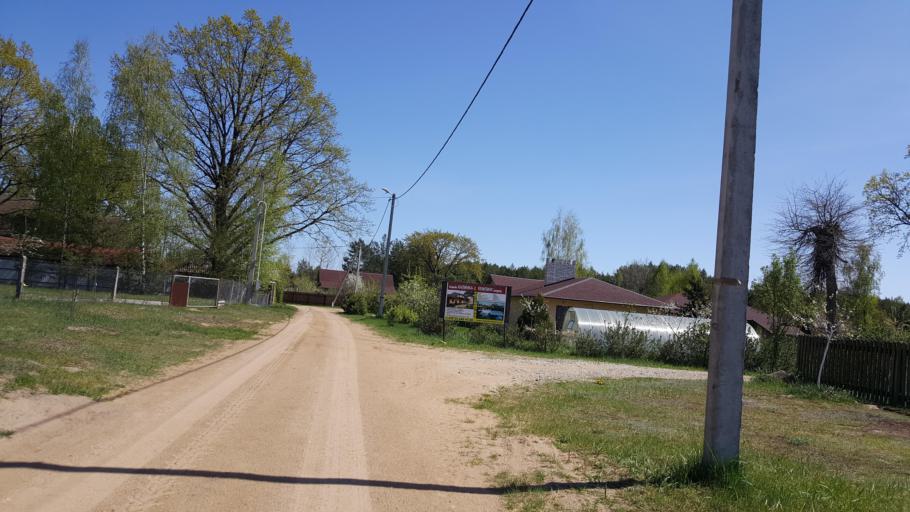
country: BY
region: Brest
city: Kamyanyets
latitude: 52.4265
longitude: 23.8492
